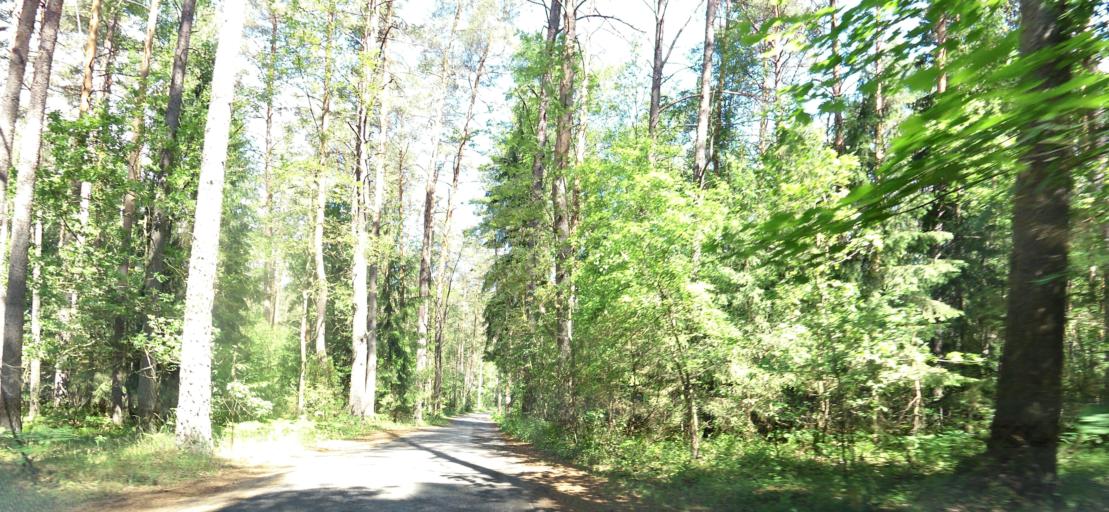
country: LT
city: Nemencine
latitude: 54.8100
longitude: 25.3939
